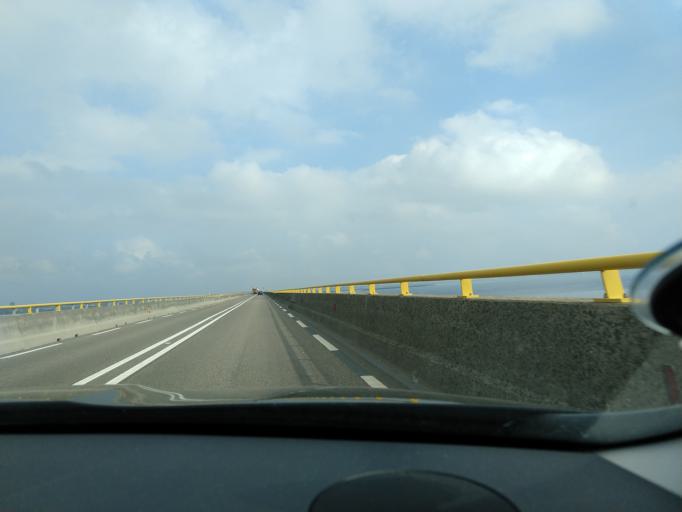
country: NL
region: Zeeland
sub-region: Gemeente Goes
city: Goes
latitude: 51.6186
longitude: 3.8999
